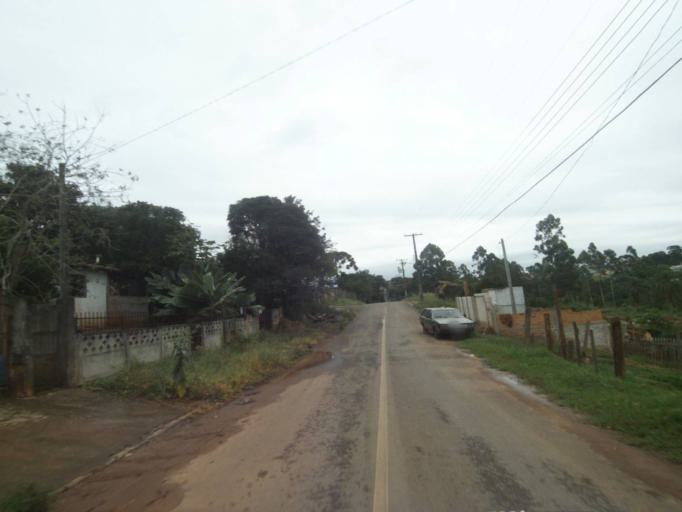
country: BR
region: Parana
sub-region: Telemaco Borba
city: Telemaco Borba
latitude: -24.3183
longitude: -50.6539
